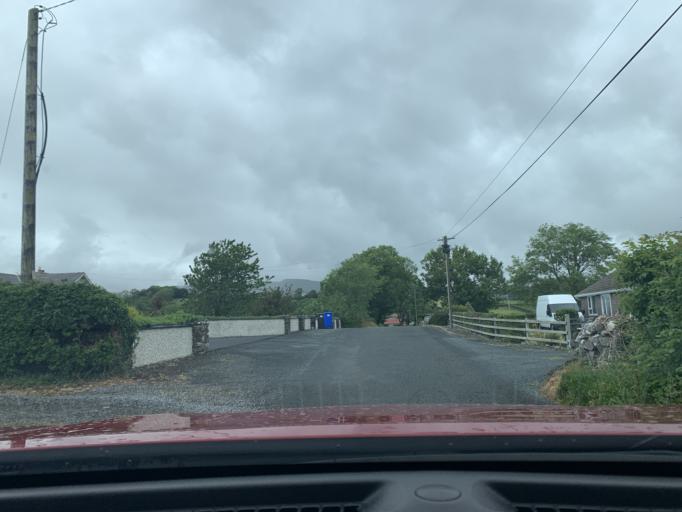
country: IE
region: Connaught
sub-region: Sligo
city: Sligo
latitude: 54.3006
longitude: -8.4582
